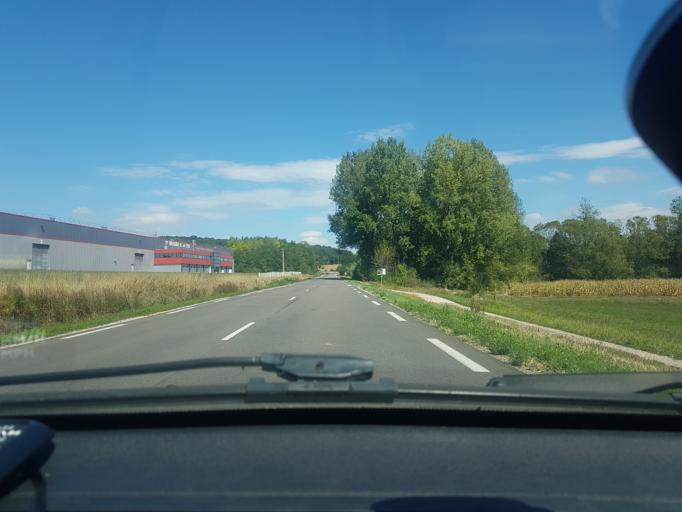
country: FR
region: Franche-Comte
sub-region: Departement de la Haute-Saone
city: Gray-la-Ville
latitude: 47.4420
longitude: 5.5484
